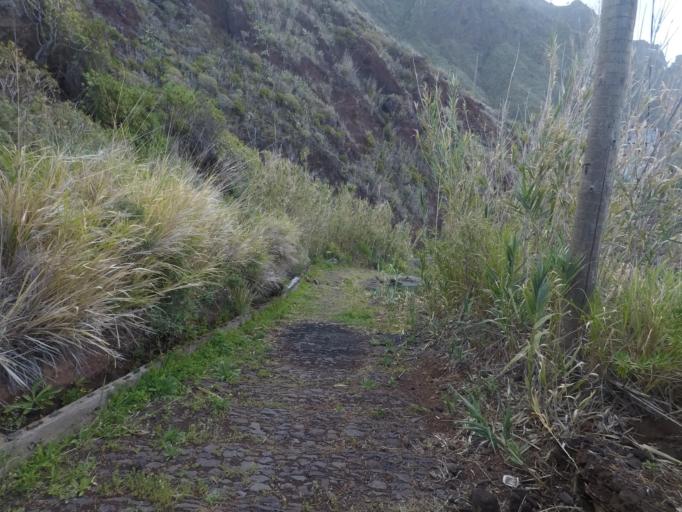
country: PT
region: Madeira
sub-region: Calheta
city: Faja da Ovelha
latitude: 32.7661
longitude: -17.2354
